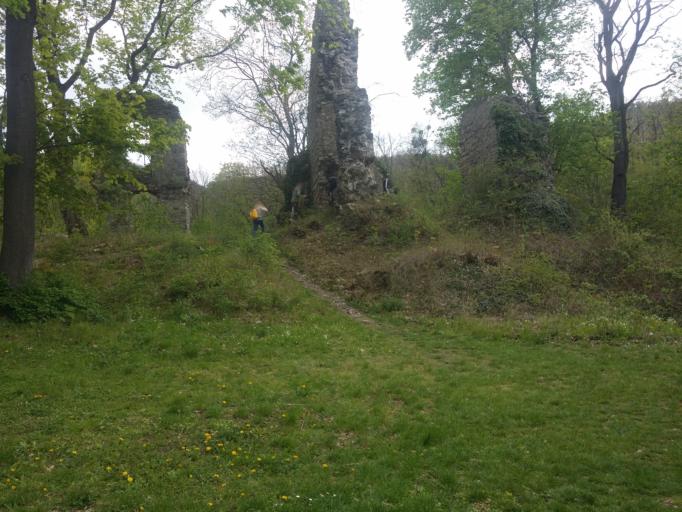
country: DE
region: Saxony-Anhalt
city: Neinstedt
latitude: 51.7329
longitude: 11.0868
